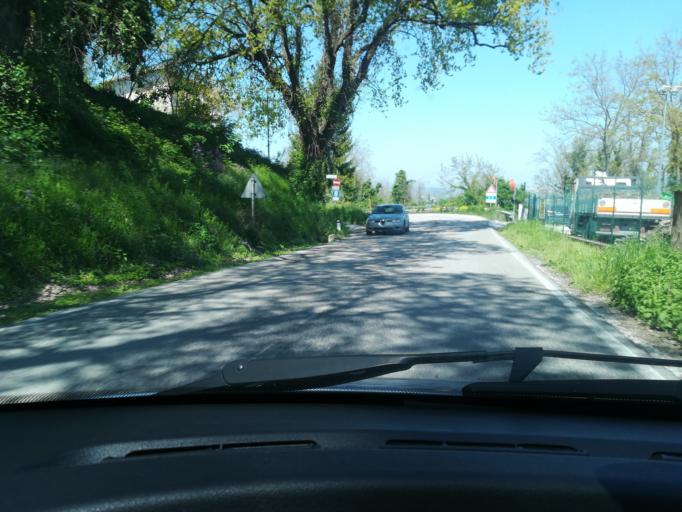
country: IT
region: The Marches
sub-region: Provincia di Macerata
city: Cingoli
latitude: 43.3787
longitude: 13.2159
